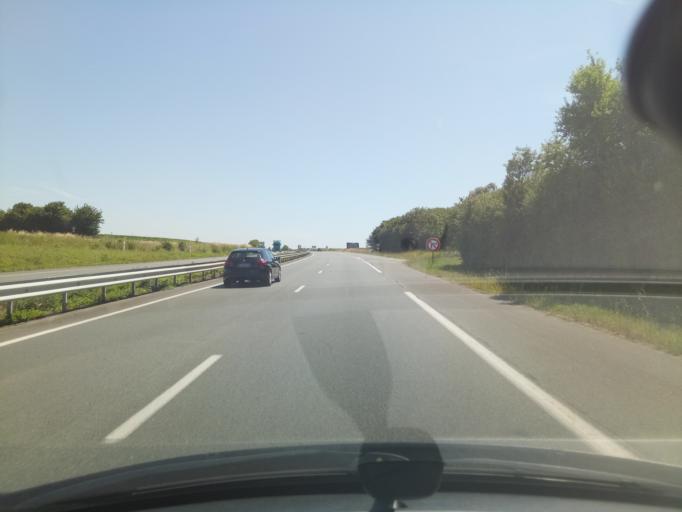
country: FR
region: Poitou-Charentes
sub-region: Departement de la Charente-Maritime
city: Dompierre-sur-Mer
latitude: 46.1976
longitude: -1.0482
